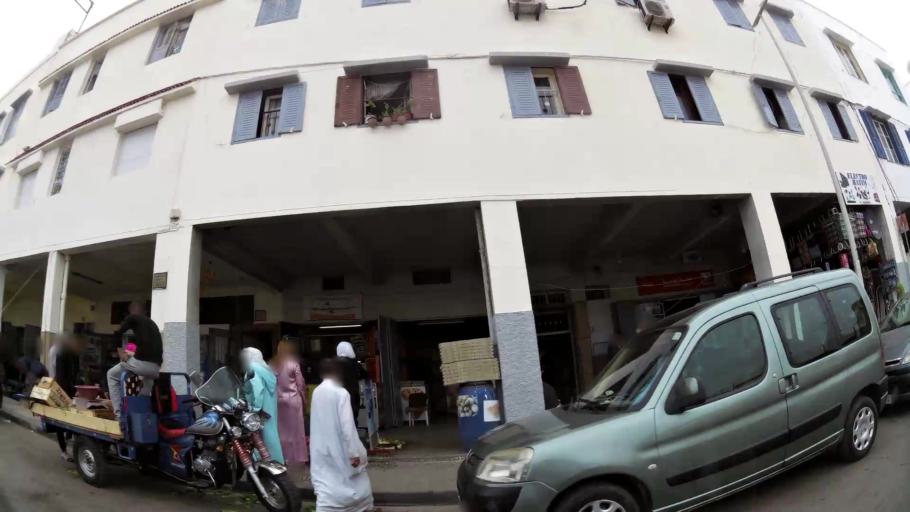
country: MA
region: Rabat-Sale-Zemmour-Zaer
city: Sale
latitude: 34.0445
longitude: -6.8071
